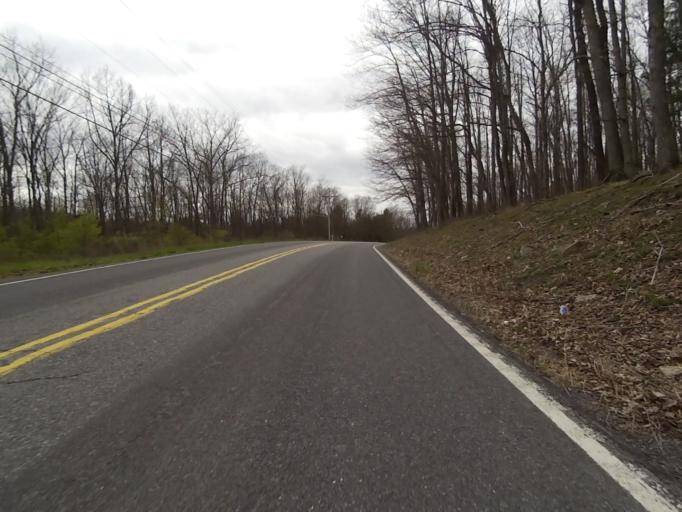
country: US
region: Pennsylvania
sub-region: Clearfield County
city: Troy
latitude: 40.9066
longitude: -78.1136
